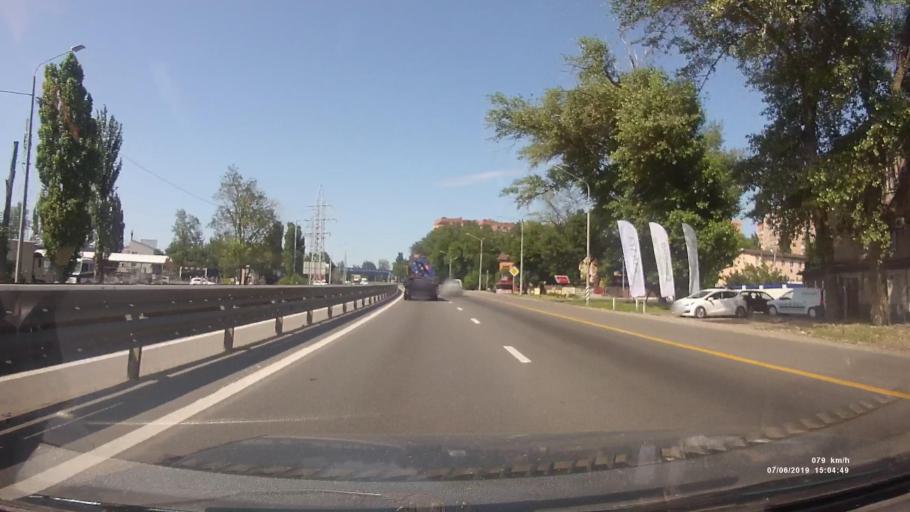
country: RU
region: Rostov
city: Aksay
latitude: 47.2659
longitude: 39.8543
